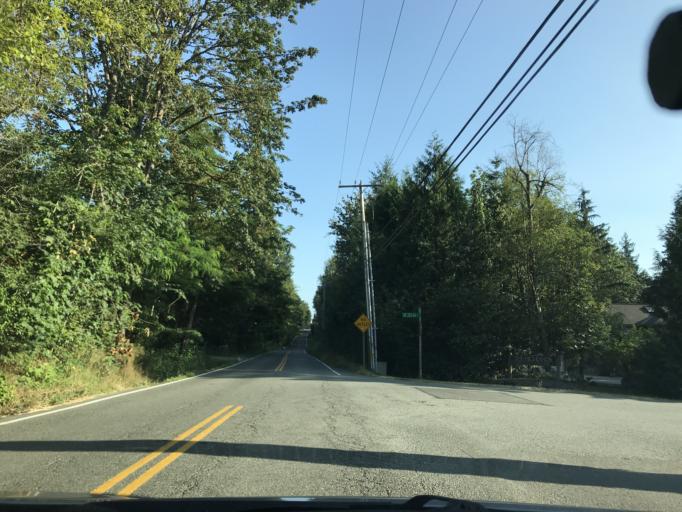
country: US
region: Washington
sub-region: King County
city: Maple Valley
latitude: 47.4003
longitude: -122.0164
